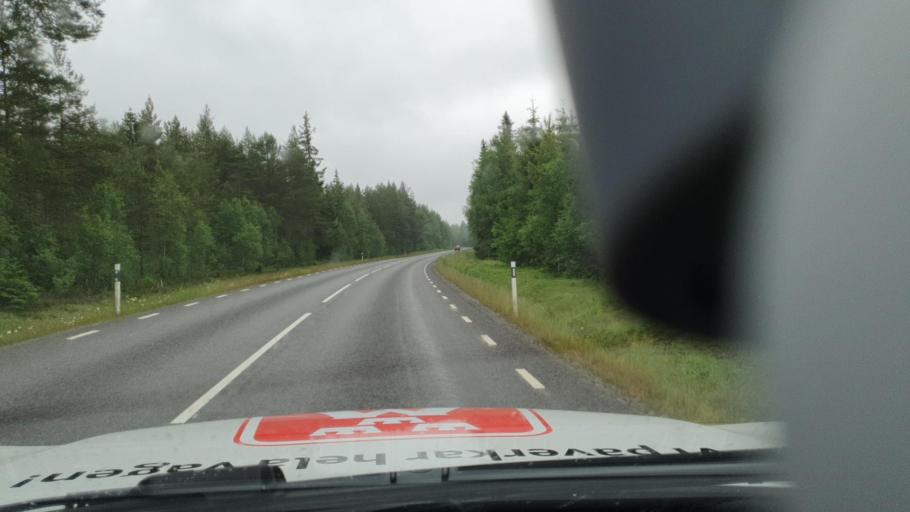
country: SE
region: Vaermland
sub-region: Kristinehamns Kommun
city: Bjorneborg
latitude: 59.2259
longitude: 14.3069
